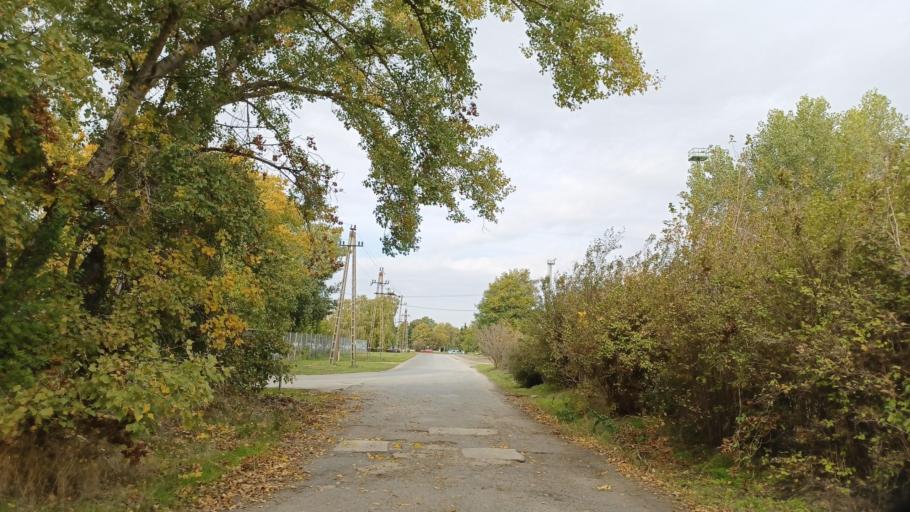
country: HU
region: Tolna
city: Paks
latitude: 46.6056
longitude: 18.8523
